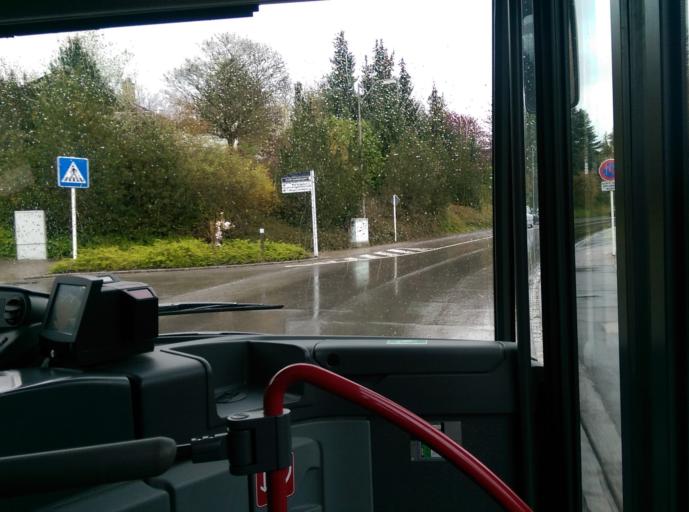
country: LU
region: Luxembourg
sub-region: Canton de Luxembourg
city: Niederanven
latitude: 49.6582
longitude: 6.2485
